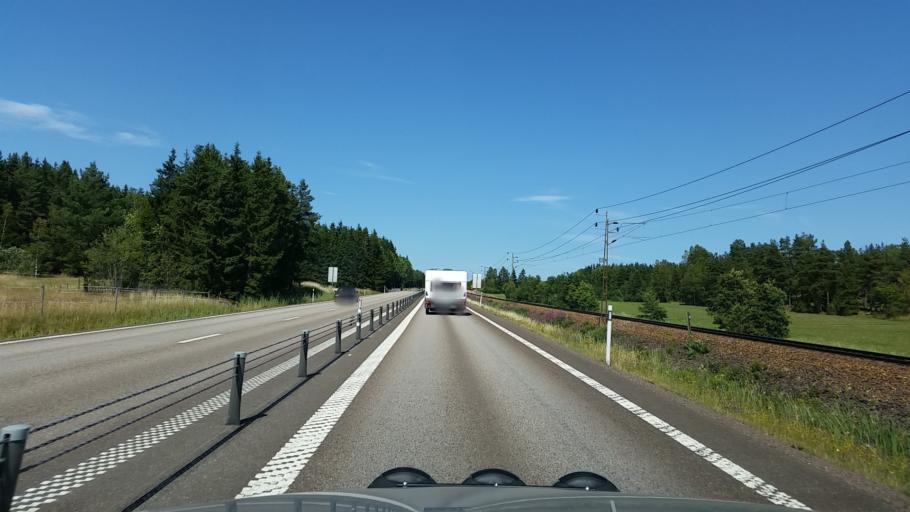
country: SE
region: Vaestra Goetaland
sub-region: Melleruds Kommun
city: Mellerud
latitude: 58.8578
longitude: 12.5576
